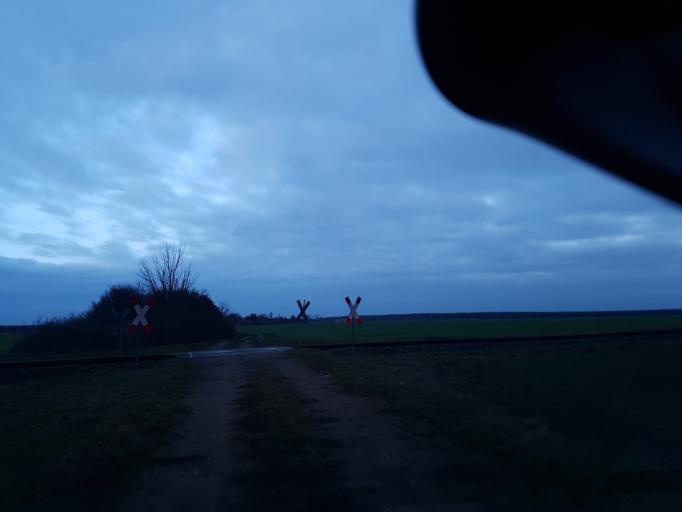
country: DE
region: Brandenburg
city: Muhlberg
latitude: 51.4653
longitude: 13.2683
